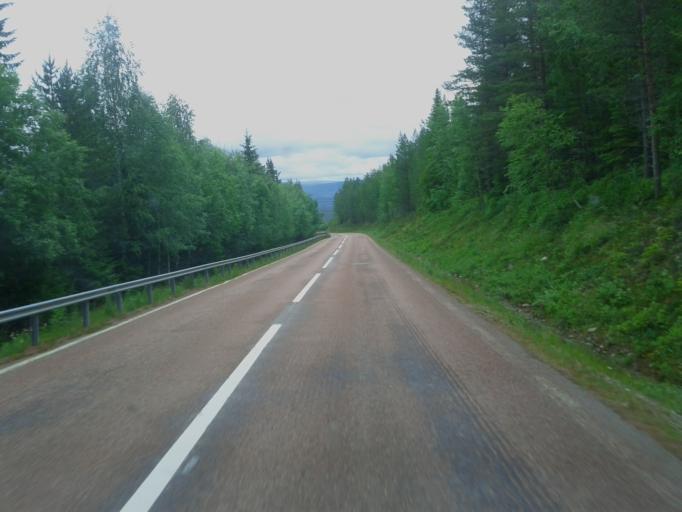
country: NO
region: Hedmark
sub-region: Trysil
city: Innbygda
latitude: 61.8478
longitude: 12.6049
